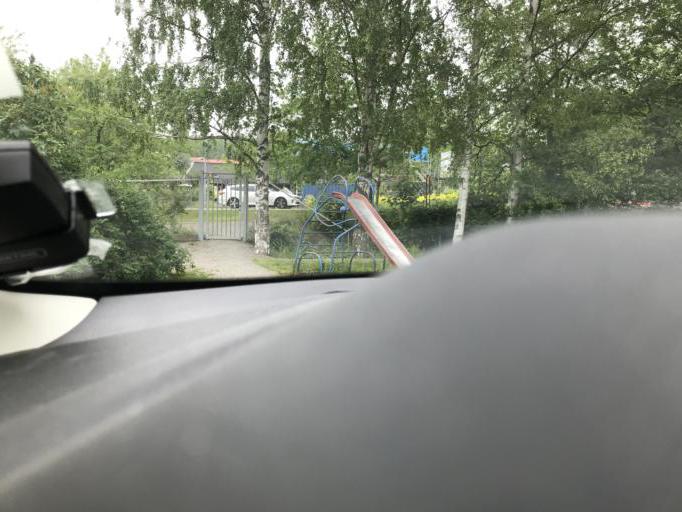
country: SE
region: Stockholm
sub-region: Botkyrka Kommun
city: Tumba
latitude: 59.2118
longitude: 17.8230
